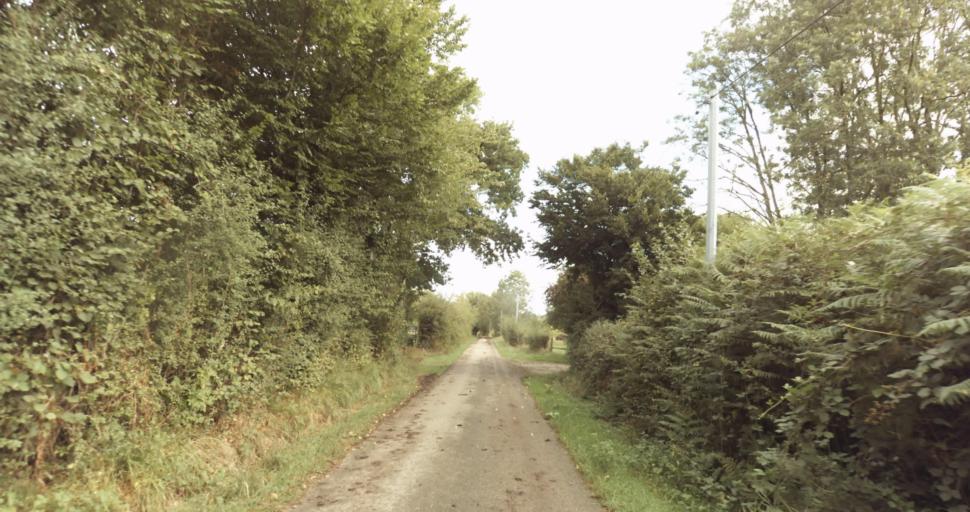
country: FR
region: Lower Normandy
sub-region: Departement de l'Orne
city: Gace
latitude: 48.8096
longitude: 0.2513
